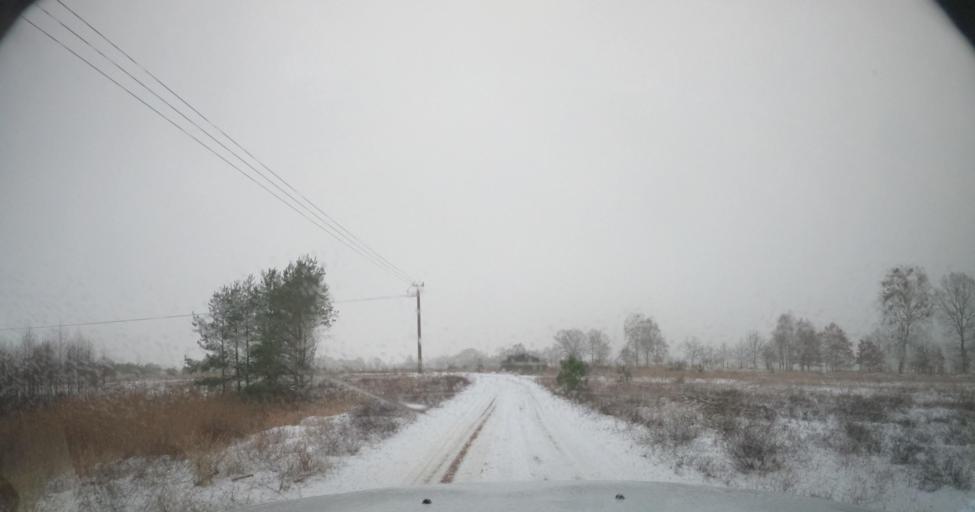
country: PL
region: West Pomeranian Voivodeship
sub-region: Powiat kamienski
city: Golczewo
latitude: 53.7810
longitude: 14.9580
